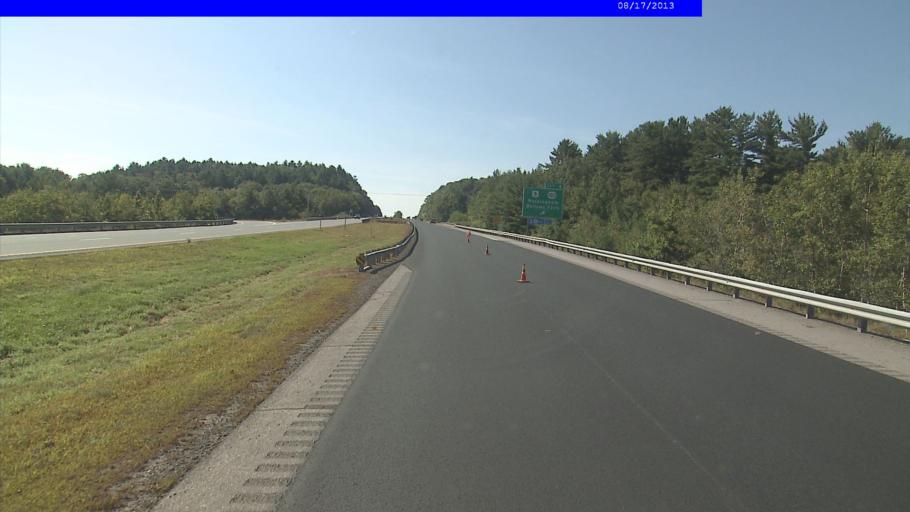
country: US
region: Vermont
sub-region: Windham County
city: Rockingham
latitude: 43.1806
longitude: -72.4634
